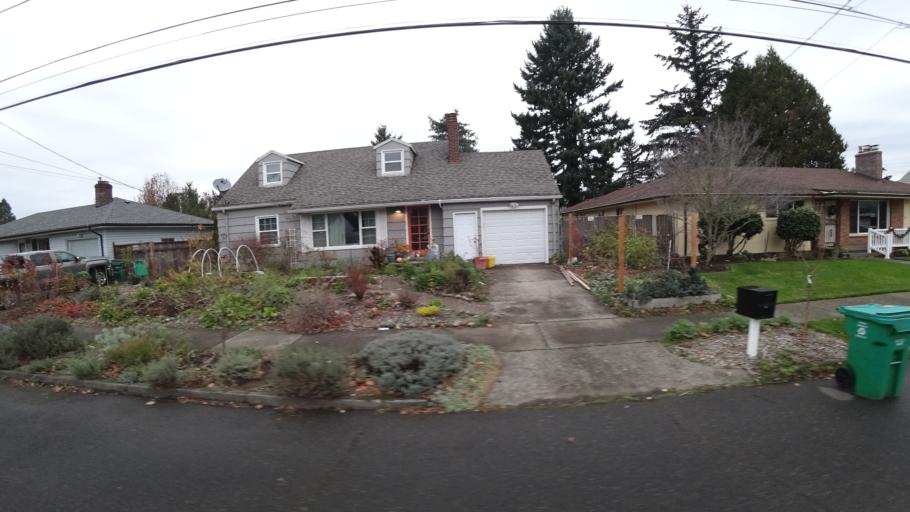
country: US
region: Oregon
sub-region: Multnomah County
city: Lents
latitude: 45.5158
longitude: -122.5333
